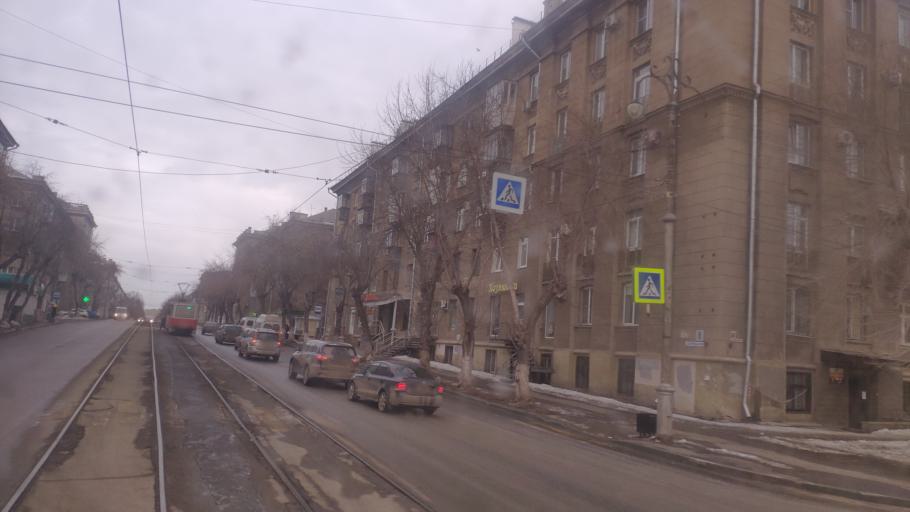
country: RU
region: Chelyabinsk
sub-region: Gorod Magnitogorsk
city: Magnitogorsk
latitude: 53.4194
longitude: 58.9981
